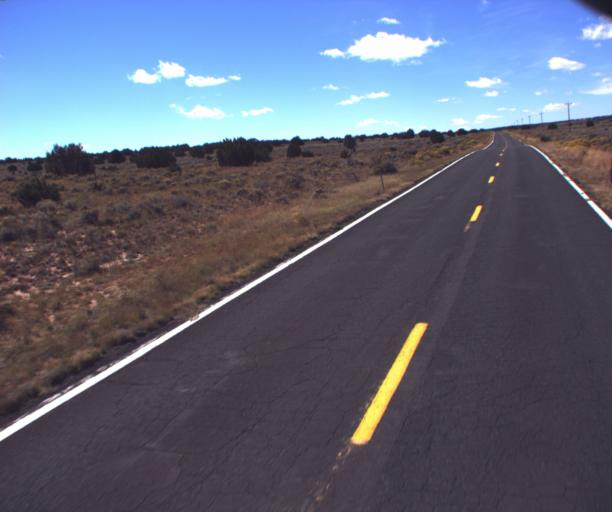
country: US
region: New Mexico
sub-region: McKinley County
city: Zuni Pueblo
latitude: 35.0034
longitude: -109.0839
